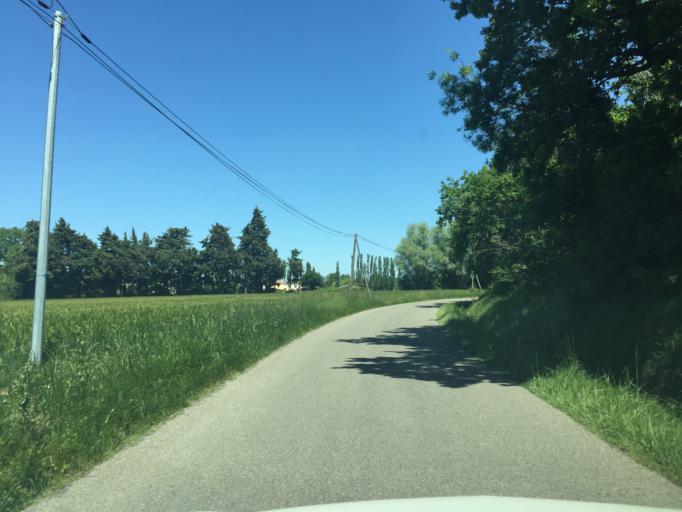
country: FR
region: Provence-Alpes-Cote d'Azur
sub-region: Departement du Vaucluse
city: Caderousse
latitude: 44.1045
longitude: 4.7630
